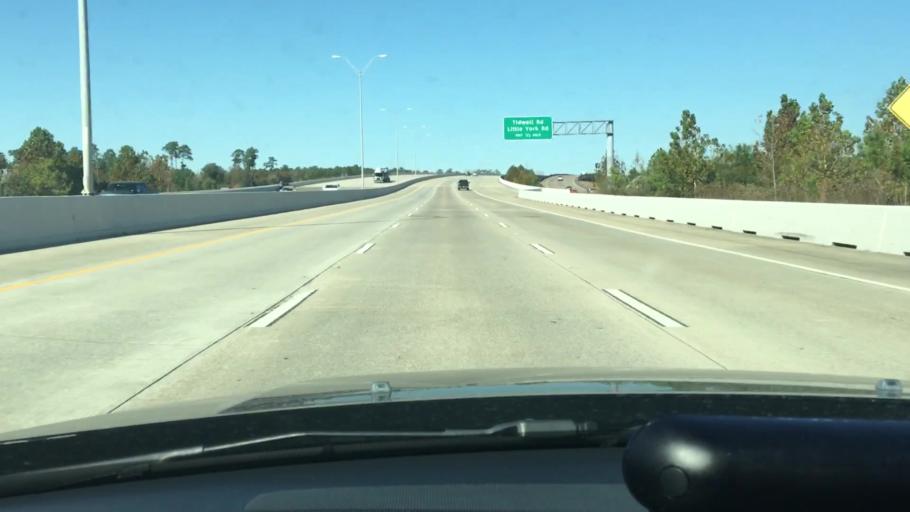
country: US
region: Texas
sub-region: Harris County
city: Sheldon
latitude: 29.8395
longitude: -95.1822
